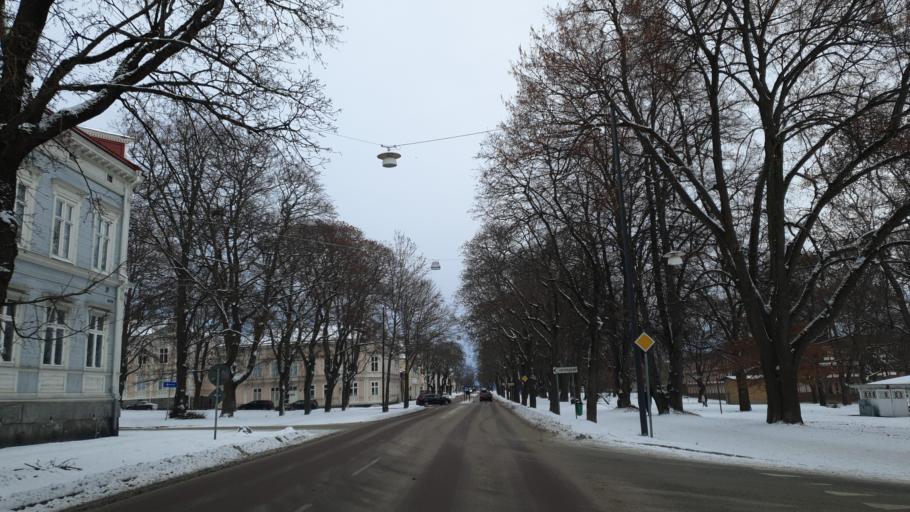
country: SE
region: Gaevleborg
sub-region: Soderhamns Kommun
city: Soderhamn
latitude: 61.3045
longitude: 17.0579
